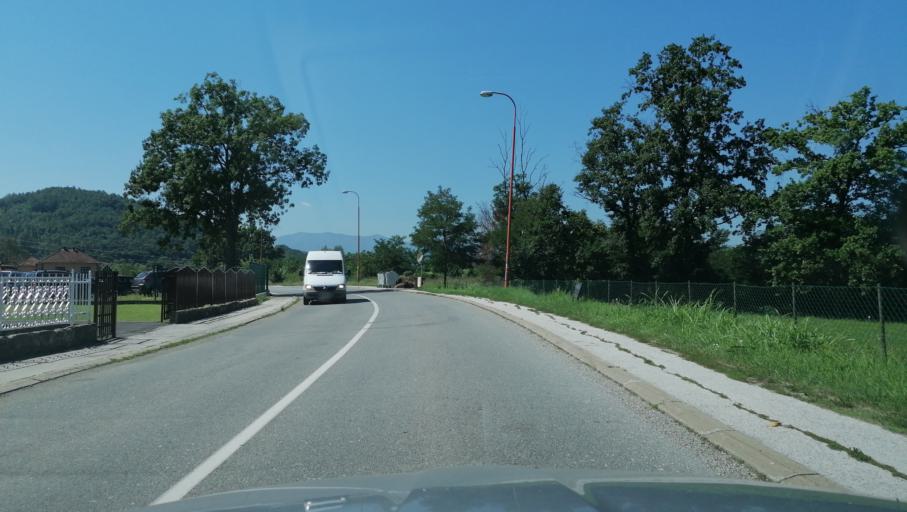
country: RS
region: Central Serbia
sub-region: Raski Okrug
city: Kraljevo
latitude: 43.6923
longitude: 20.6321
